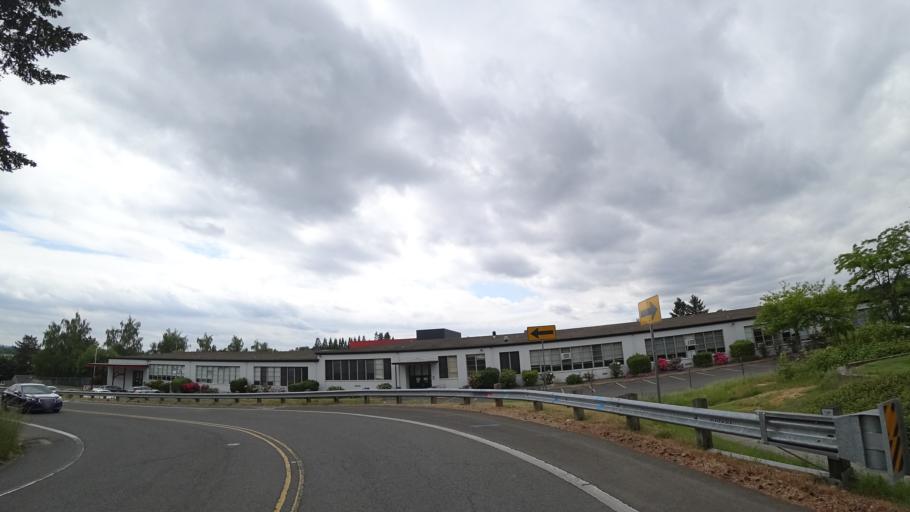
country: US
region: Oregon
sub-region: Washington County
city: Cedar Hills
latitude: 45.4949
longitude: -122.7931
